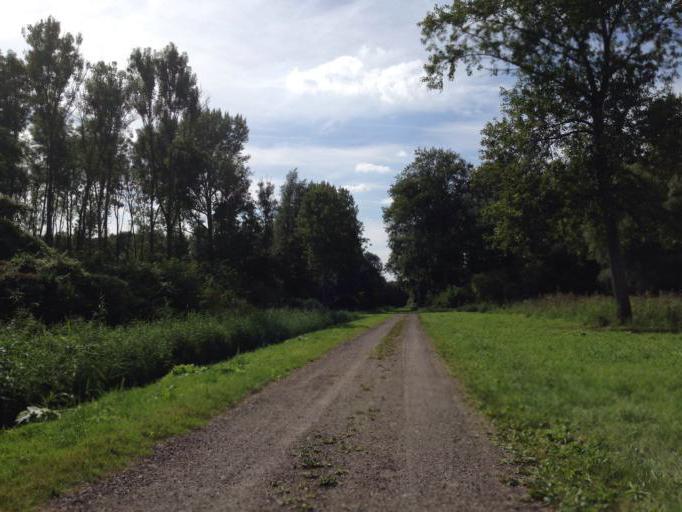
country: NL
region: North Holland
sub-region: Gemeente Huizen
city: Huizen
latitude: 52.3476
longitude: 5.2679
